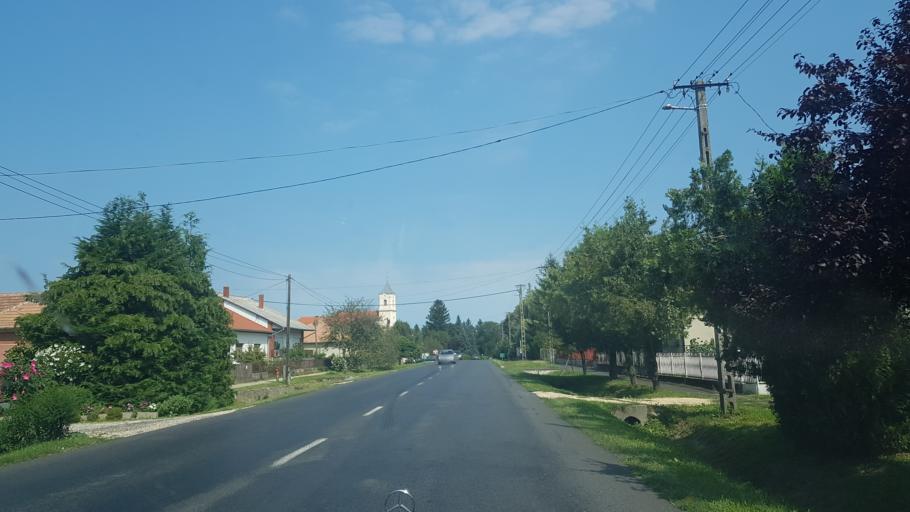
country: HU
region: Somogy
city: Bohonye
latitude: 46.4938
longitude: 17.4238
